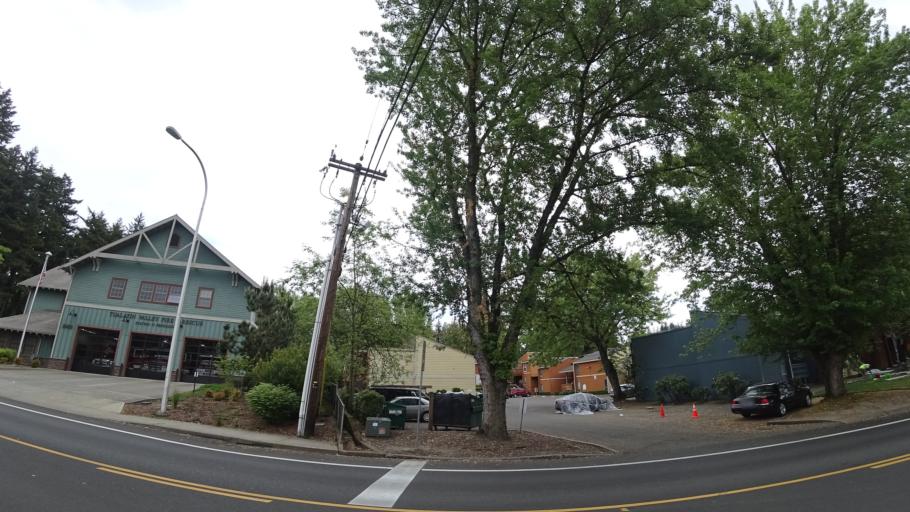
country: US
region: Oregon
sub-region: Washington County
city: Garden Home-Whitford
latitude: 45.4586
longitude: -122.7815
